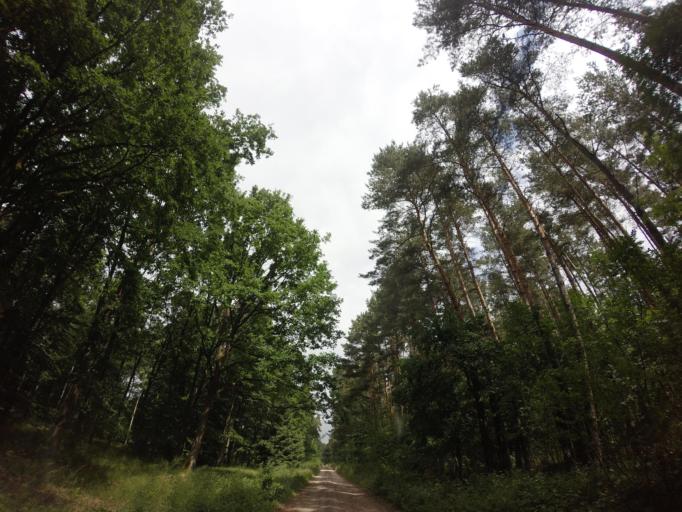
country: PL
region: West Pomeranian Voivodeship
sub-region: Powiat choszczenski
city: Krzecin
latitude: 53.0193
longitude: 15.5304
